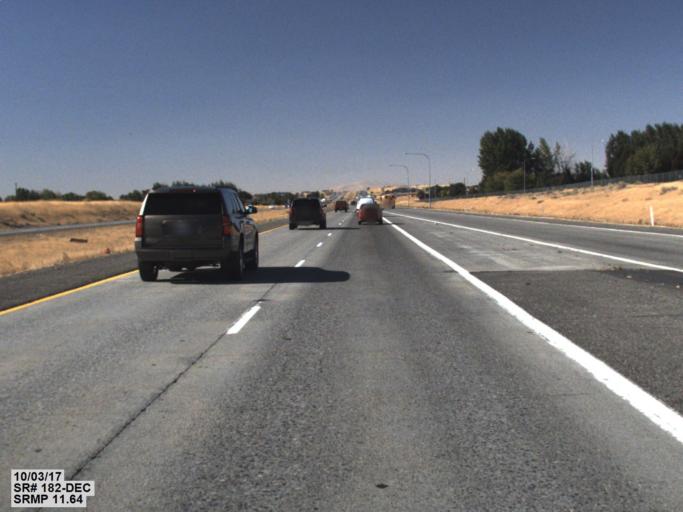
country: US
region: Washington
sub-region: Franklin County
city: Pasco
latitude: 46.2522
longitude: -119.1383
